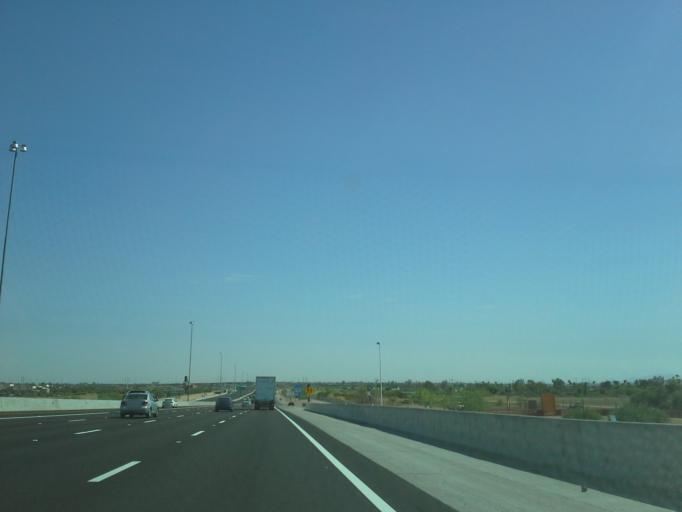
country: US
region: Arizona
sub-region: Maricopa County
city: Scottsdale
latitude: 33.4638
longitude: -111.8890
